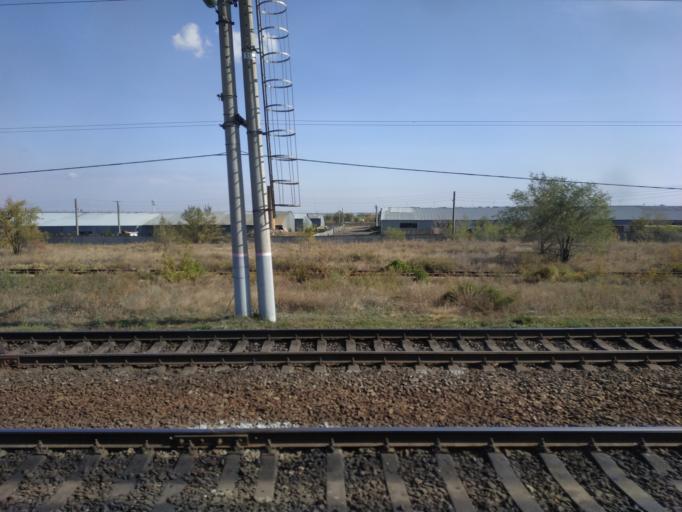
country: RU
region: Volgograd
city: Gumrak
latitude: 48.7885
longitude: 44.3695
